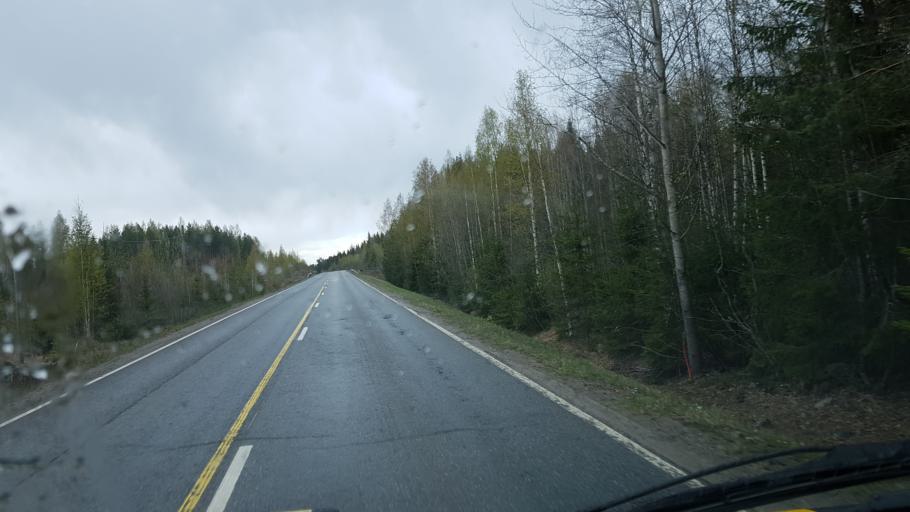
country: FI
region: Pirkanmaa
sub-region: Tampere
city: Pirkkala
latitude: 61.4025
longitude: 23.6310
